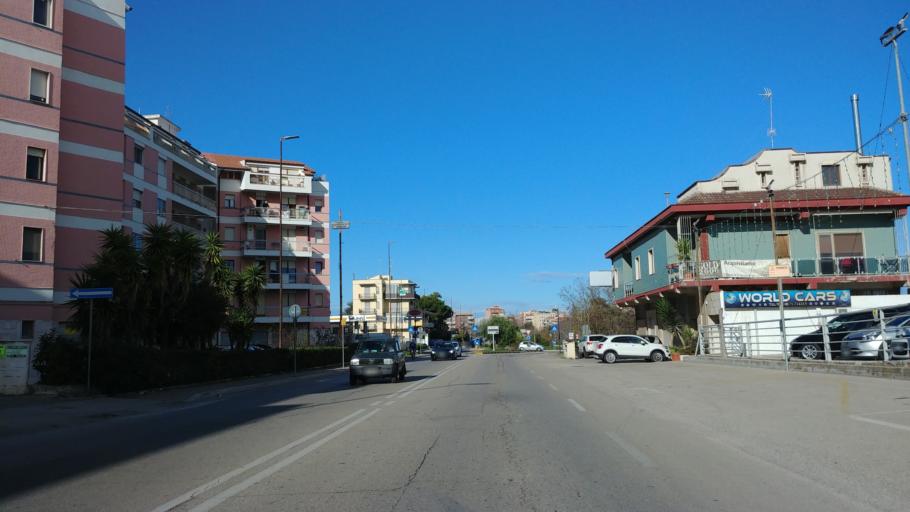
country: IT
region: Molise
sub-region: Provincia di Campobasso
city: Termoli
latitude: 41.9926
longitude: 14.9989
